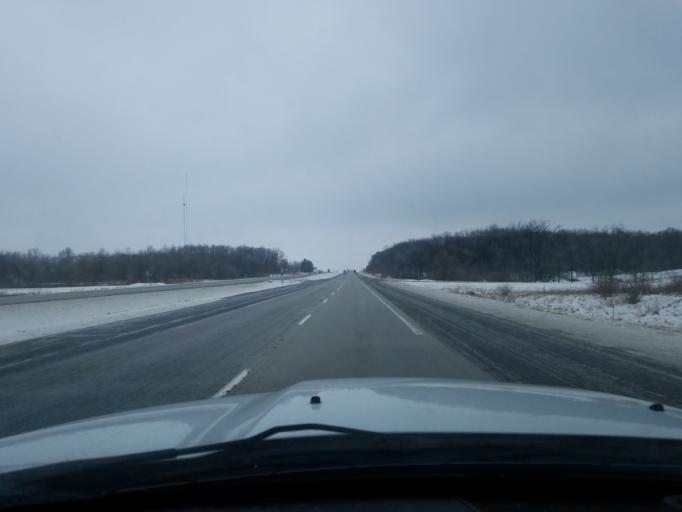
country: US
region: Indiana
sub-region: Fulton County
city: Rochester
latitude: 41.1098
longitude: -86.2397
